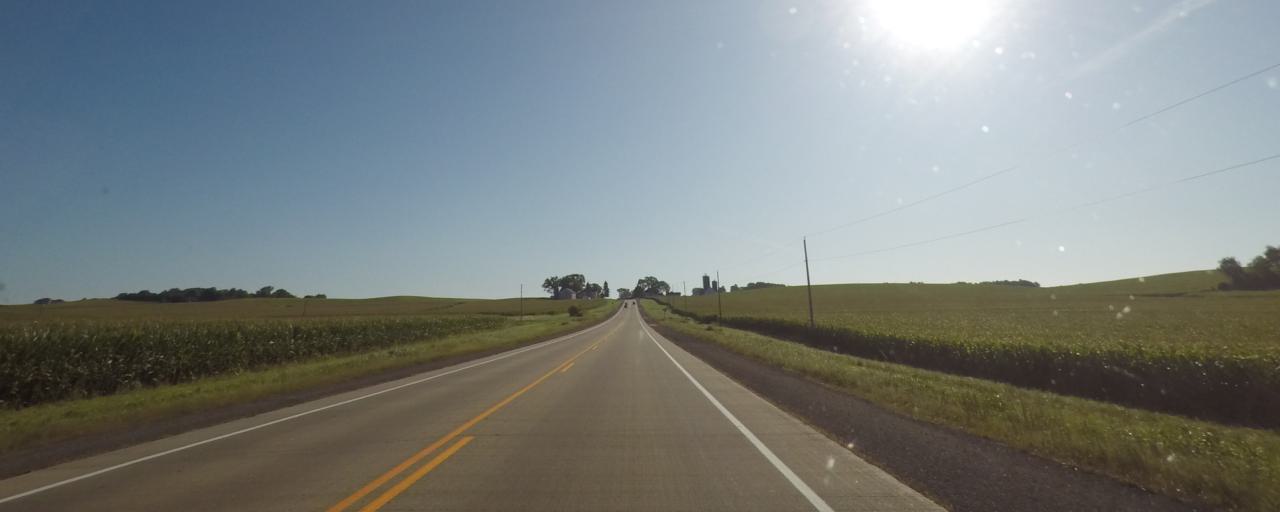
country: US
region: Wisconsin
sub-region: Dane County
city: Cottage Grove
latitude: 43.0290
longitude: -89.1636
